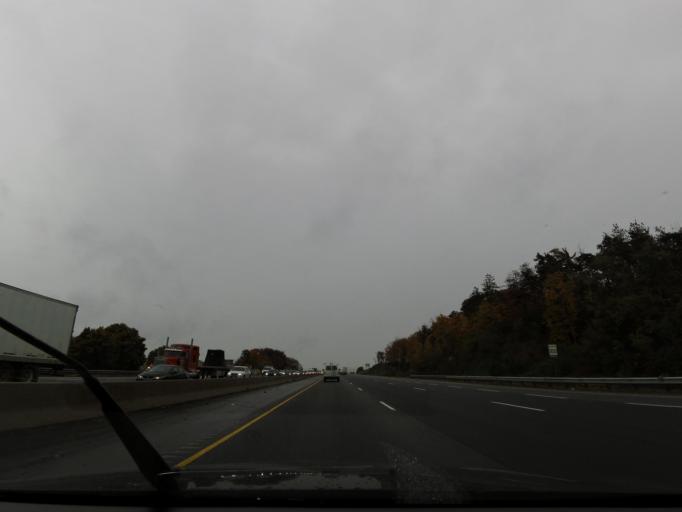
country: CA
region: Ontario
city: Cambridge
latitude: 43.4143
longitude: -80.3185
